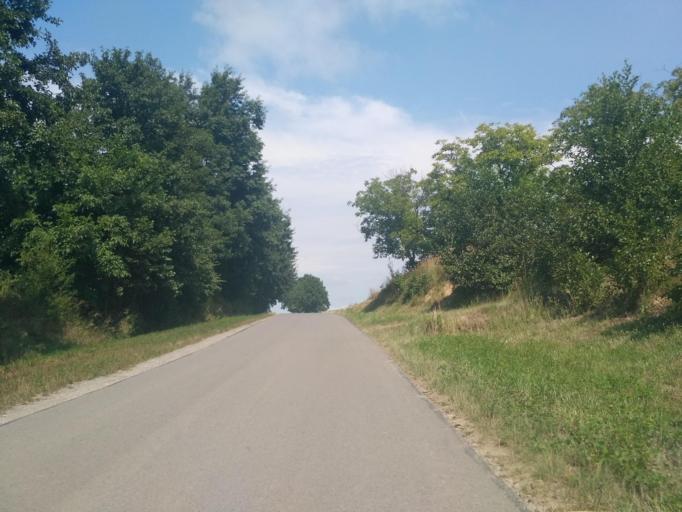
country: PL
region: Subcarpathian Voivodeship
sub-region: Powiat lancucki
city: Krzemienica
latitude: 50.0453
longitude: 22.1957
